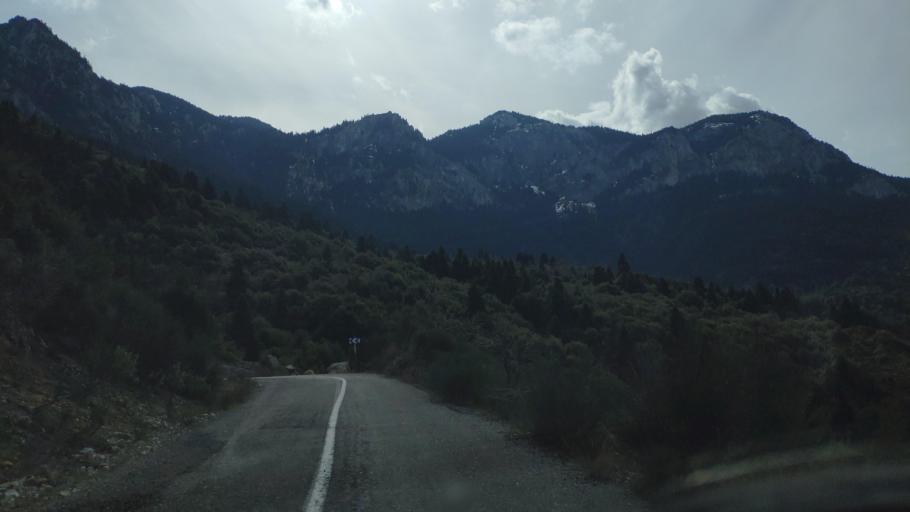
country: GR
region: Central Greece
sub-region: Nomos Fokidos
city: Amfissa
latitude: 38.6398
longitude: 22.4192
